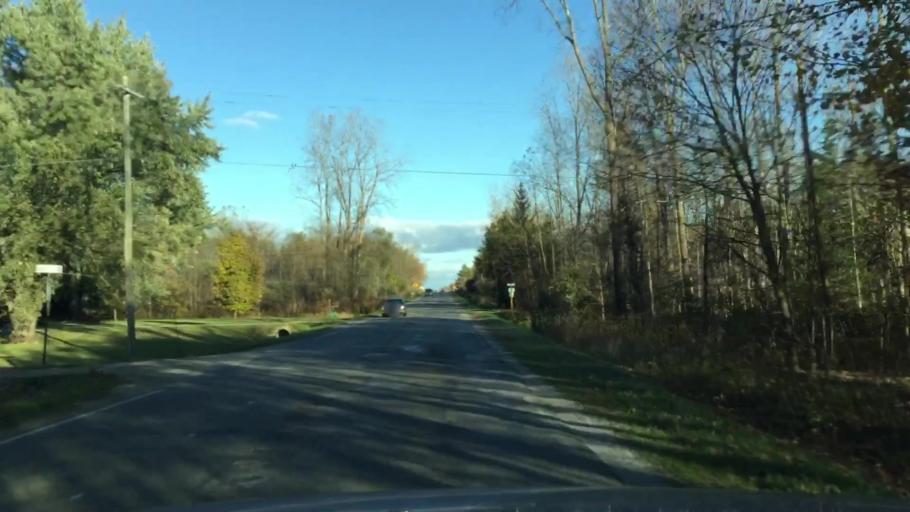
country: US
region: Michigan
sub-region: Lapeer County
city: Imlay City
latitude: 43.0624
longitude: -83.1748
